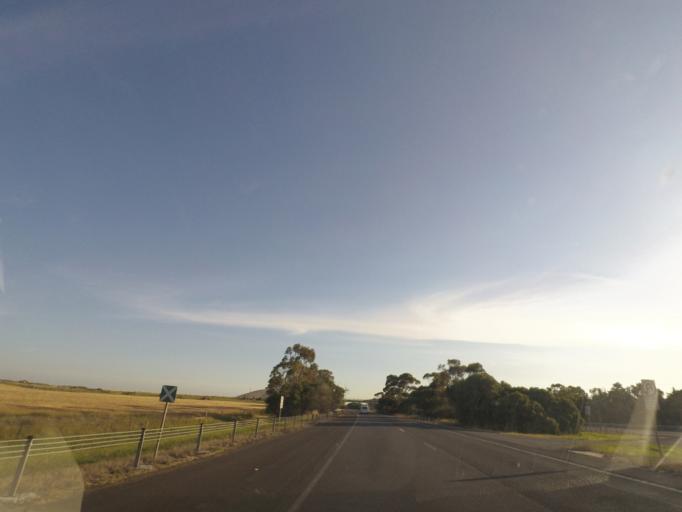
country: AU
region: Victoria
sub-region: Whittlesea
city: Whittlesea
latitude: -37.4328
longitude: 144.9829
